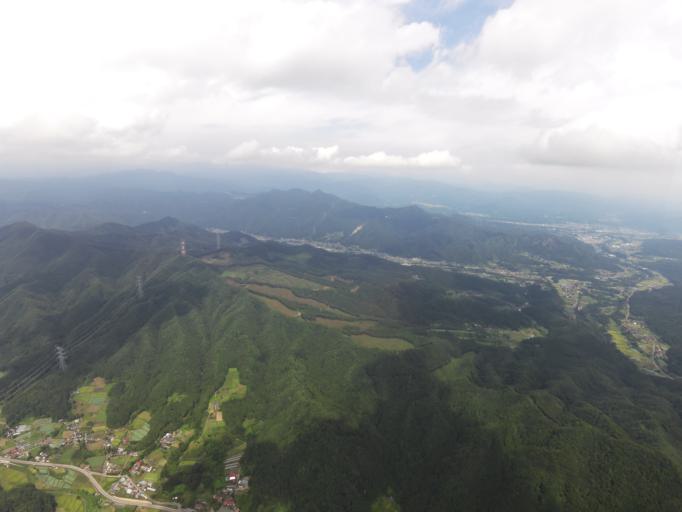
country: JP
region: Gunma
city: Nakanojomachi
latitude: 36.5175
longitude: 138.7559
